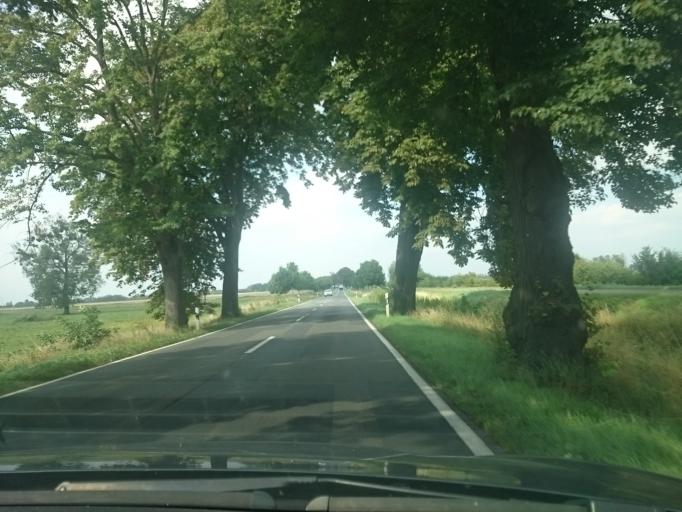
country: DE
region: Mecklenburg-Vorpommern
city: Ducherow
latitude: 53.7428
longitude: 13.7837
